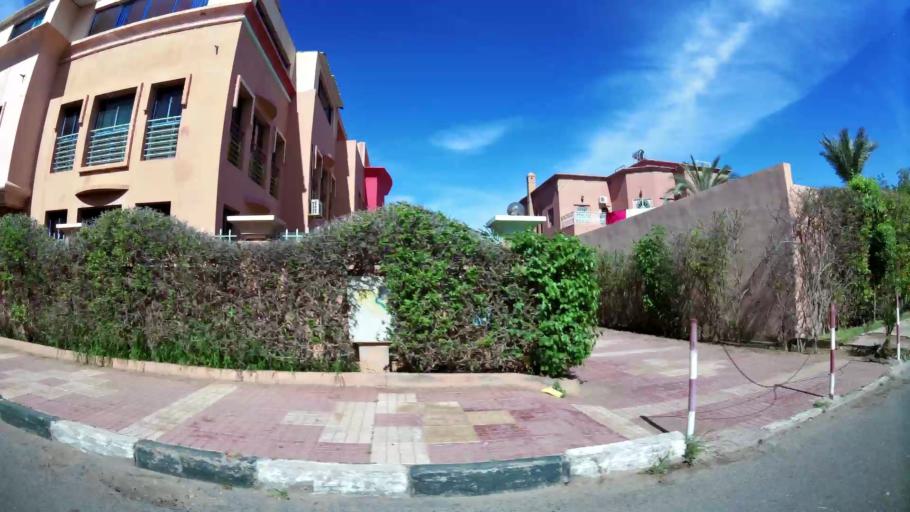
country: MA
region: Marrakech-Tensift-Al Haouz
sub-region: Marrakech
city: Marrakesh
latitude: 31.6539
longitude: -8.0526
